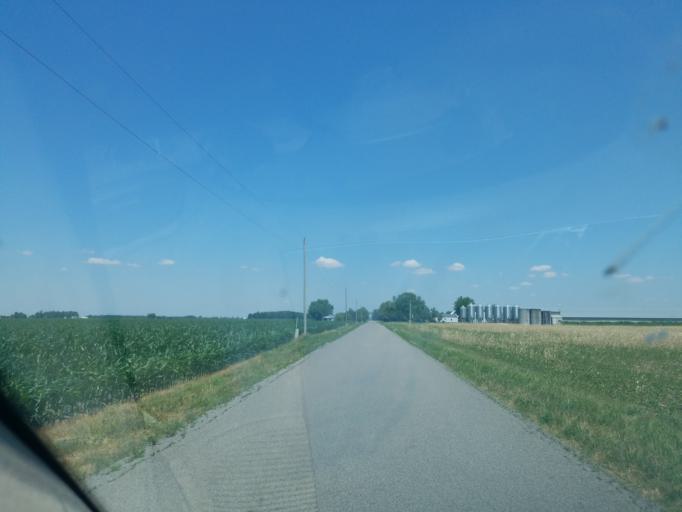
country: US
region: Ohio
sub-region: Allen County
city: Spencerville
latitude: 40.7605
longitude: -84.3494
